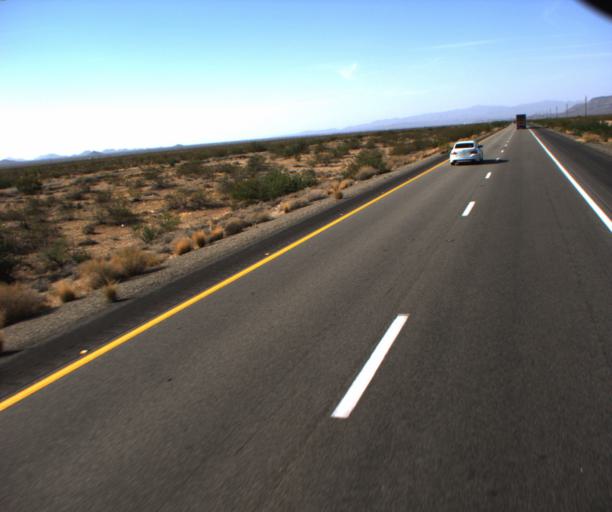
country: US
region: Arizona
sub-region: Mohave County
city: Kingman
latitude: 34.9533
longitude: -114.1458
